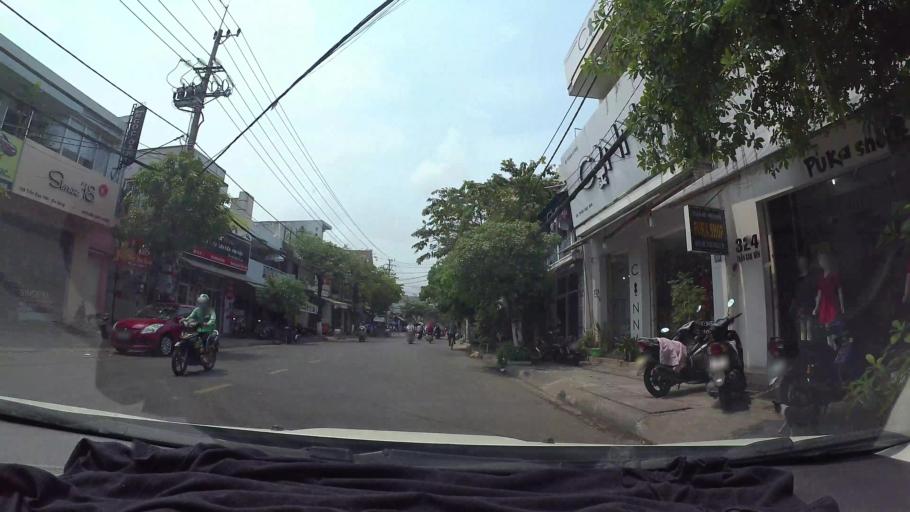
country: VN
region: Da Nang
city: Thanh Khe
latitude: 16.0715
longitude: 108.2021
